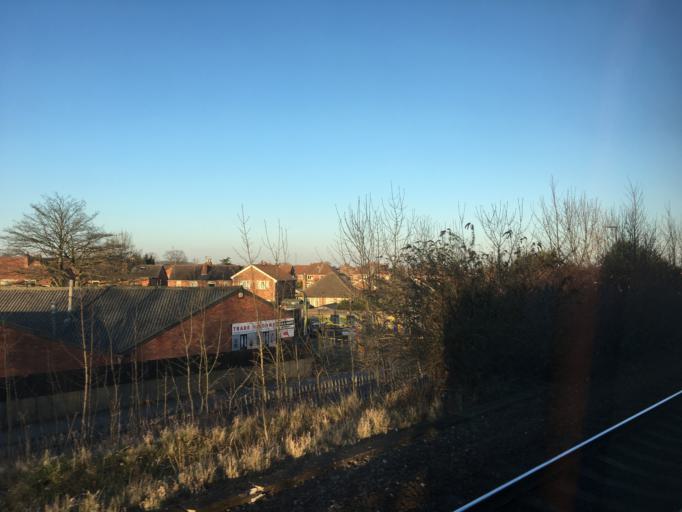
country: GB
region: England
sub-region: Derbyshire
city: Long Eaton
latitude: 52.8849
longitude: -1.2843
